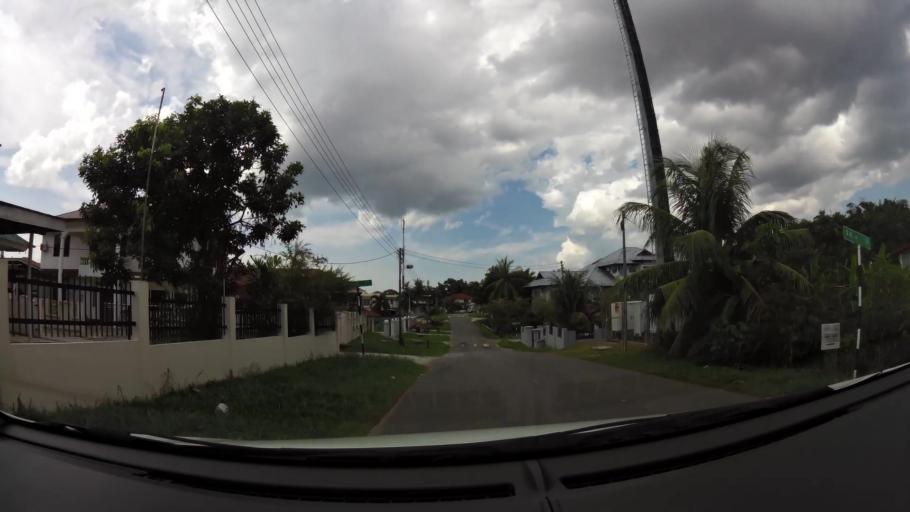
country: BN
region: Brunei and Muara
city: Bandar Seri Begawan
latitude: 4.9564
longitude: 114.9640
